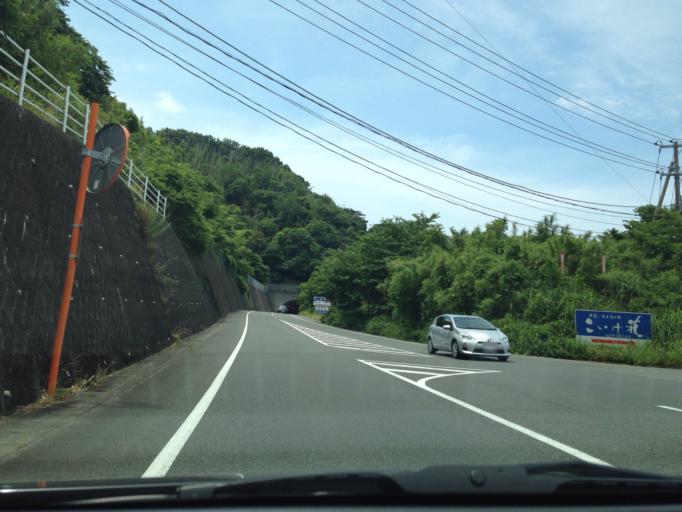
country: JP
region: Shizuoka
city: Heda
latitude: 34.8988
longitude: 138.7794
